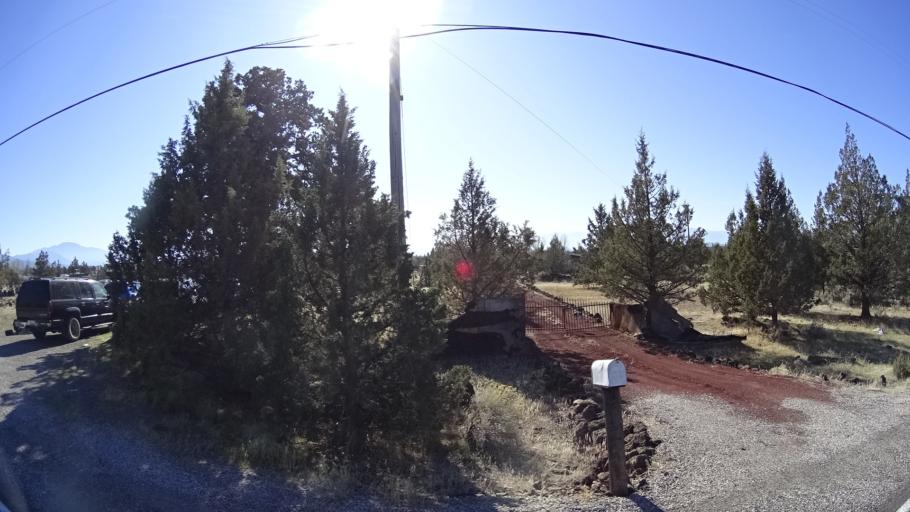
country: US
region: California
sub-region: Siskiyou County
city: Montague
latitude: 41.6597
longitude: -122.3950
